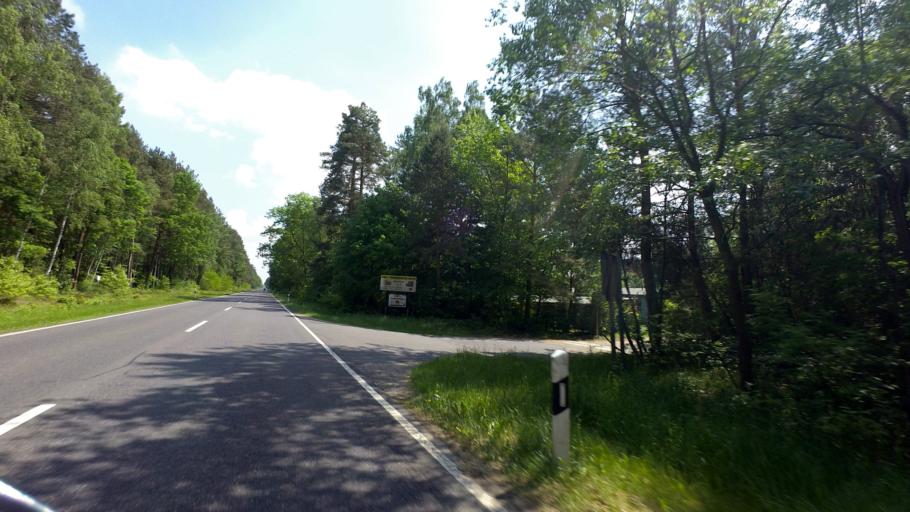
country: DE
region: Saxony
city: Schleife
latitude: 51.5514
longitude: 14.5092
